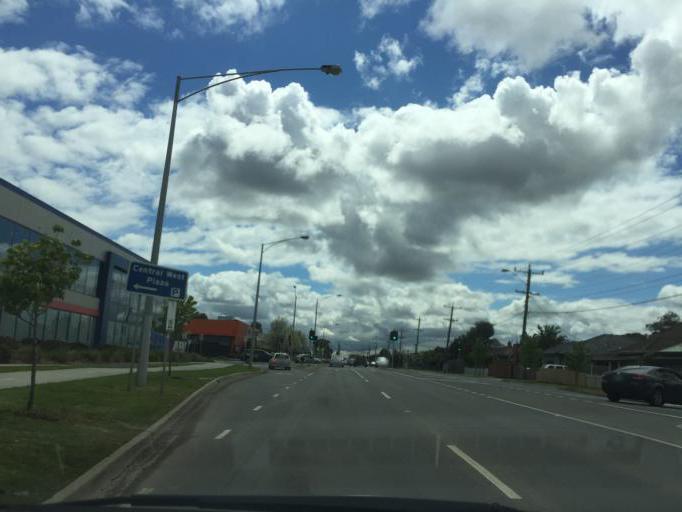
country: AU
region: Victoria
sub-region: Maribyrnong
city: Braybrook
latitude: -37.7954
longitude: 144.8627
